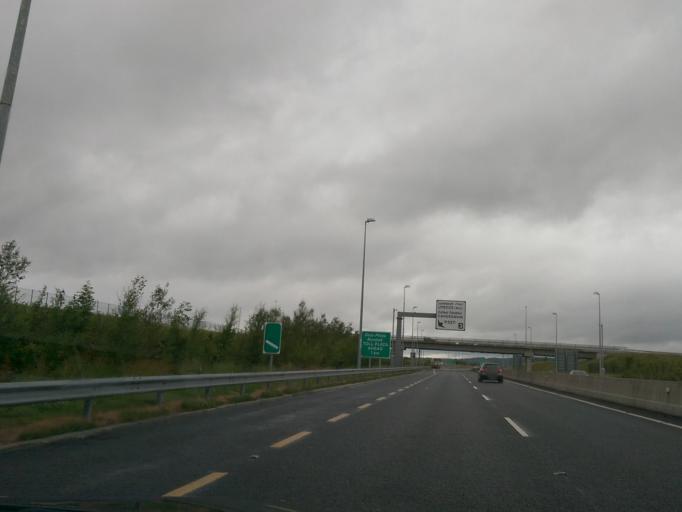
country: IE
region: Munster
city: Moyross
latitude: 52.6591
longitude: -8.6917
